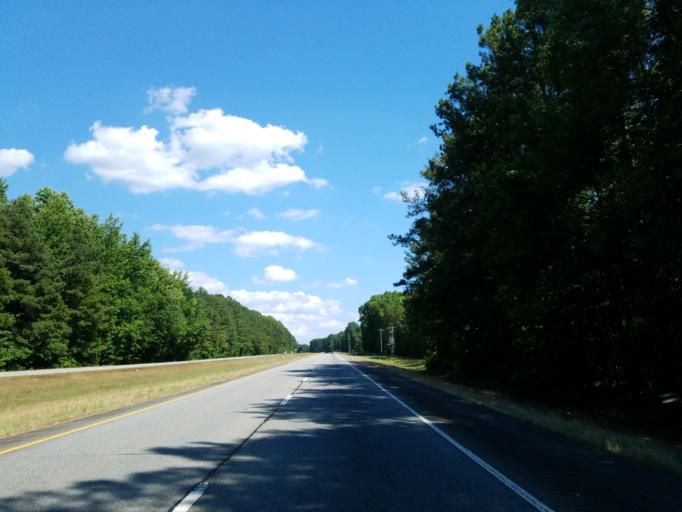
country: US
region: Georgia
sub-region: Lamar County
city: Barnesville
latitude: 33.1200
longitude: -84.2145
